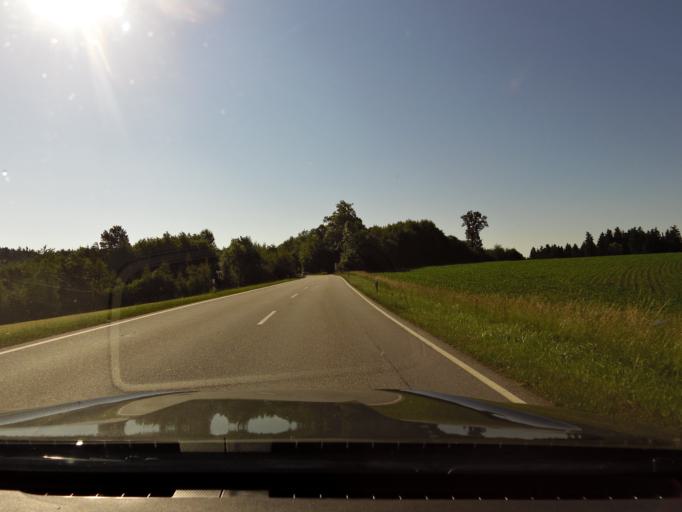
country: DE
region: Bavaria
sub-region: Upper Bavaria
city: Egglkofen
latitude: 48.4155
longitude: 12.4260
